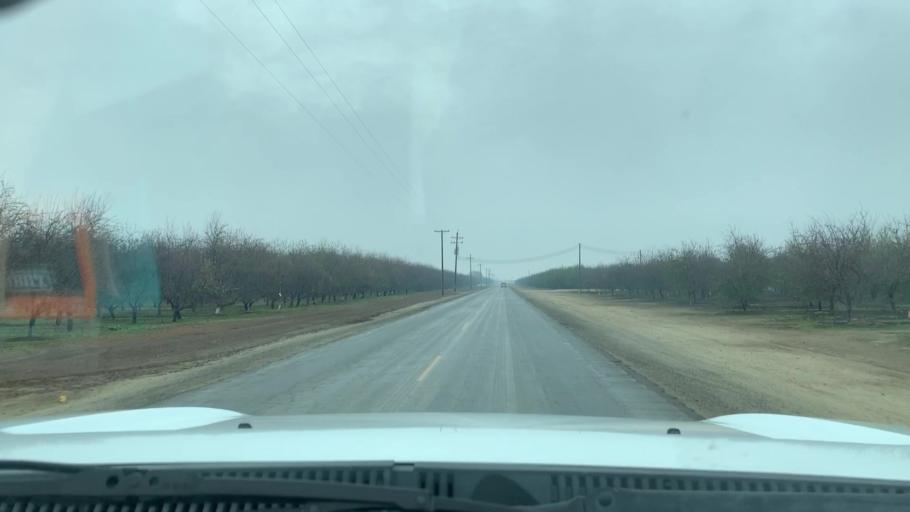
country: US
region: California
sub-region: Kern County
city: Delano
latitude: 35.7612
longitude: -119.3629
